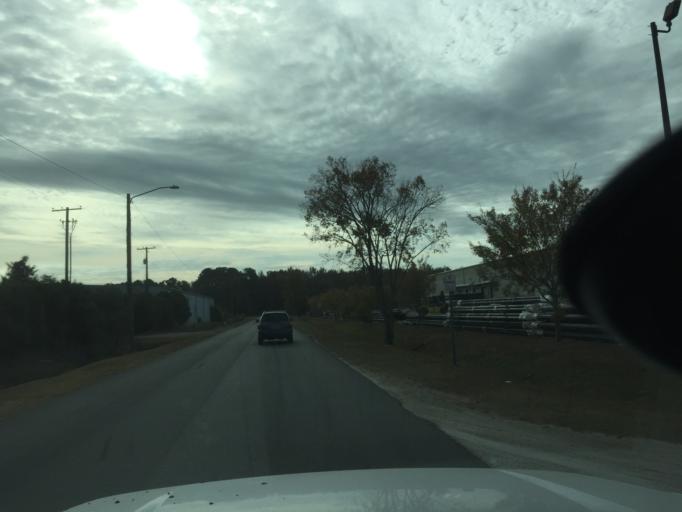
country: US
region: Georgia
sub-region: Chatham County
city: Garden City
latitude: 32.0823
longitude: -81.1463
